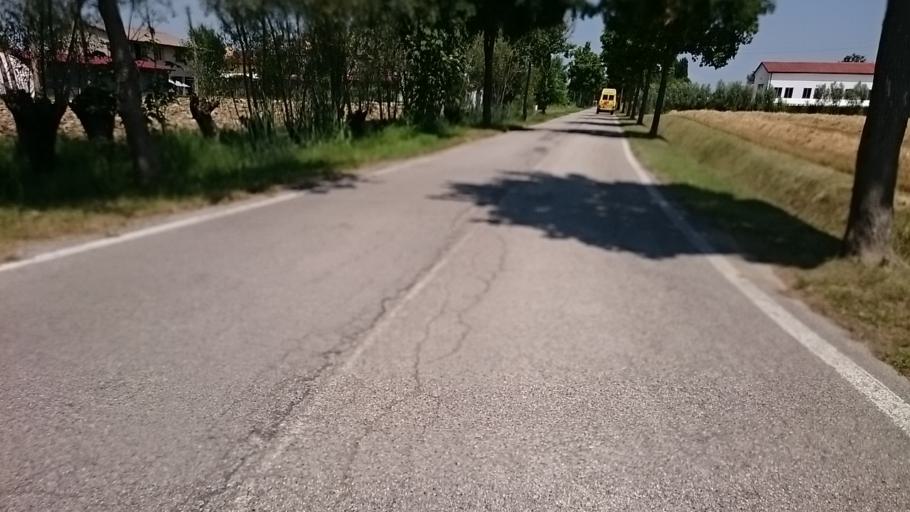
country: IT
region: Veneto
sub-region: Provincia di Venezia
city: Sant'Angelo
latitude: 45.5108
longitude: 12.0042
